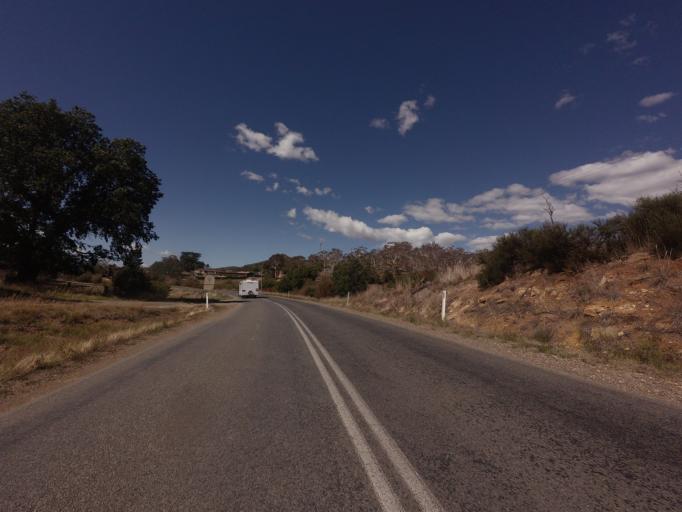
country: AU
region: Tasmania
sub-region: Break O'Day
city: St Helens
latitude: -41.6460
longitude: 147.9589
